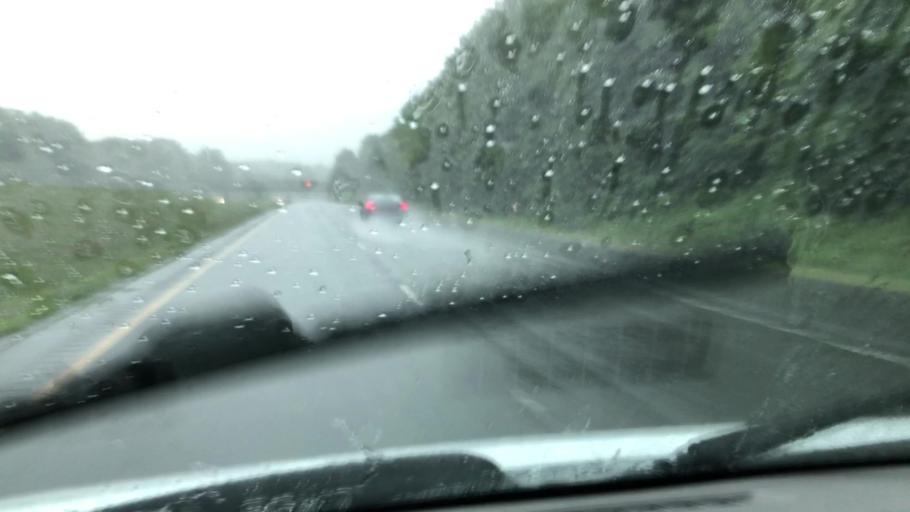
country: US
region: Massachusetts
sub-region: Hampden County
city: Westfield
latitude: 42.1551
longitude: -72.7654
